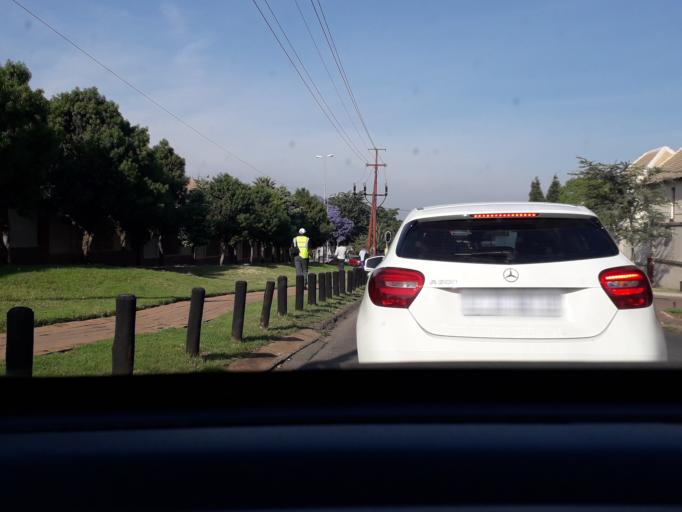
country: ZA
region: Gauteng
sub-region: City of Johannesburg Metropolitan Municipality
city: Midrand
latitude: -26.0668
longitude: 28.0568
